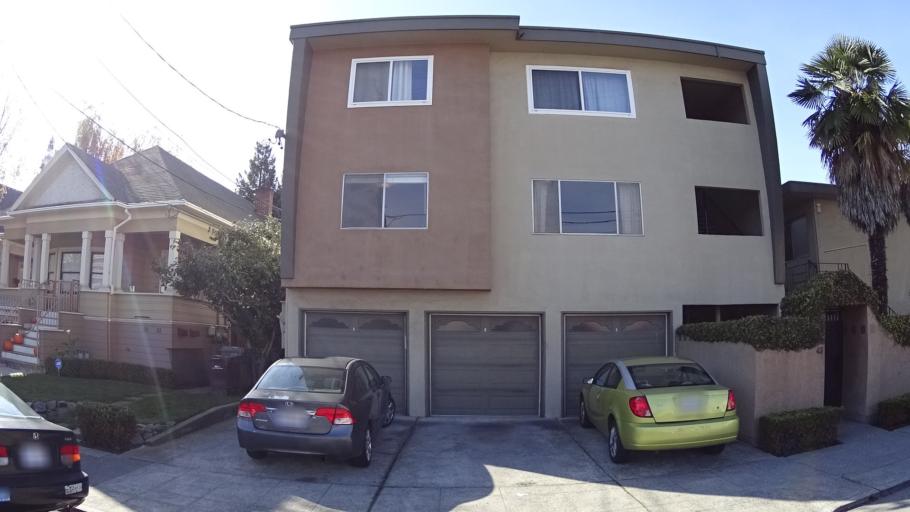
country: US
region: California
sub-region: Alameda County
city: Piedmont
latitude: 37.8251
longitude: -122.2532
